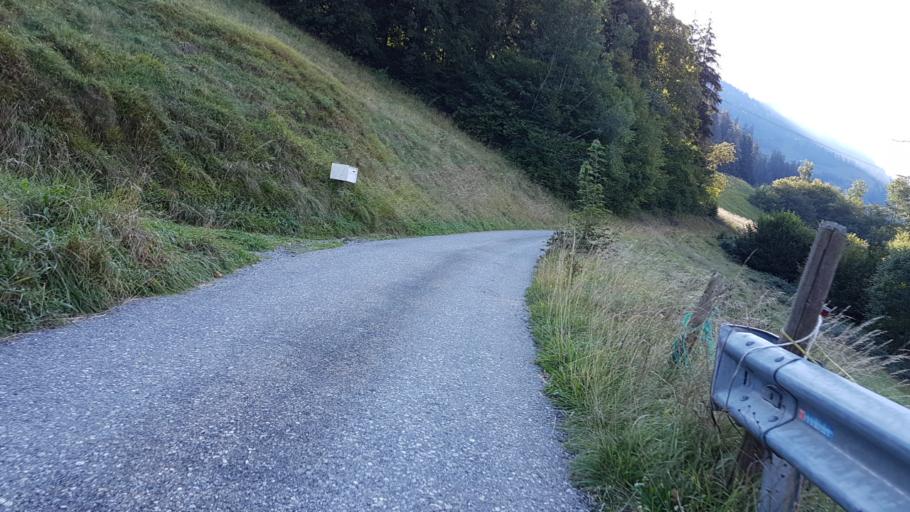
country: CH
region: Bern
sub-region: Frutigen-Niedersimmental District
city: Frutigen
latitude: 46.5643
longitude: 7.6661
